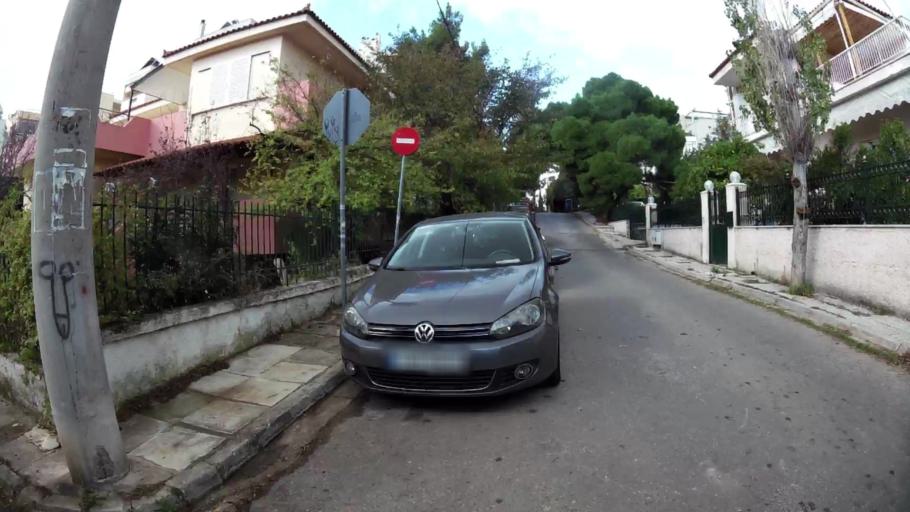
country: GR
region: Attica
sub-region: Nomarchia Athinas
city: Melissia
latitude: 38.0571
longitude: 23.8342
